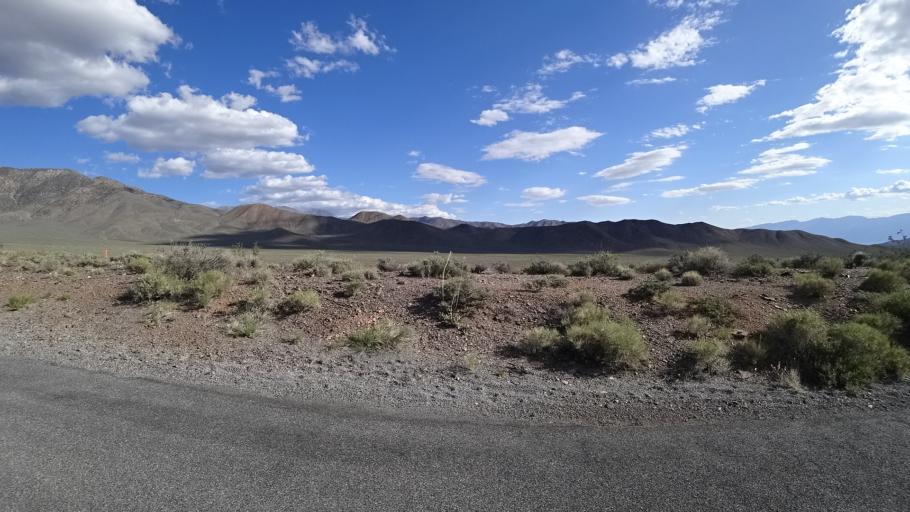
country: US
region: California
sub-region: San Bernardino County
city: Searles Valley
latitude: 36.3095
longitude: -117.1502
